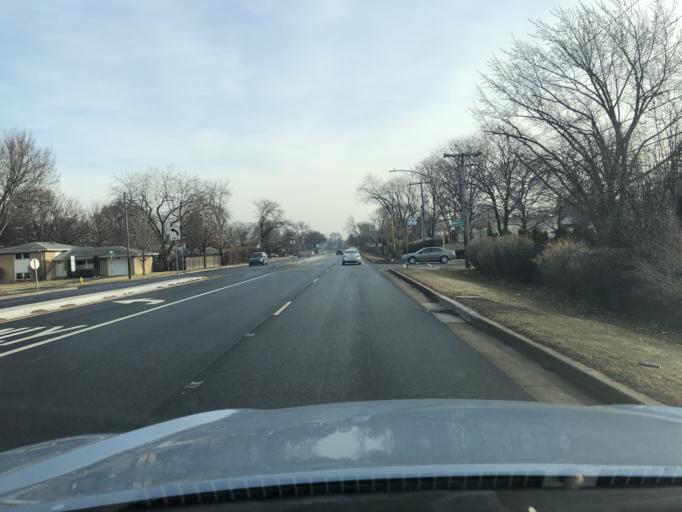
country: US
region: Illinois
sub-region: Cook County
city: Mount Prospect
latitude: 42.0477
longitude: -87.9317
